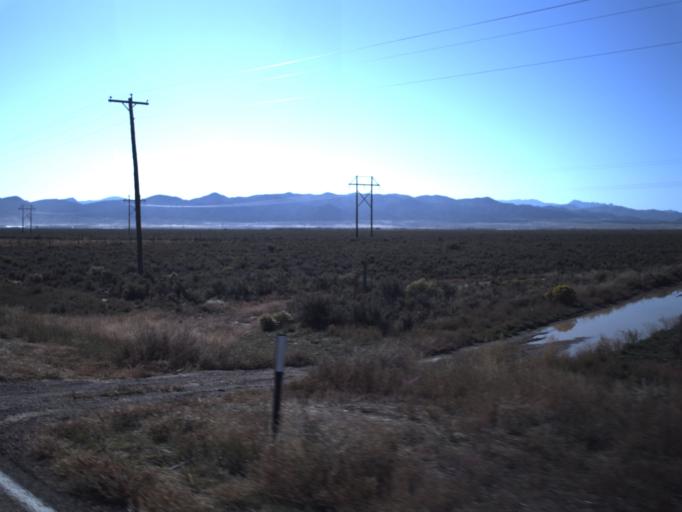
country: US
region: Utah
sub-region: Washington County
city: Enterprise
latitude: 37.7047
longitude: -113.6428
